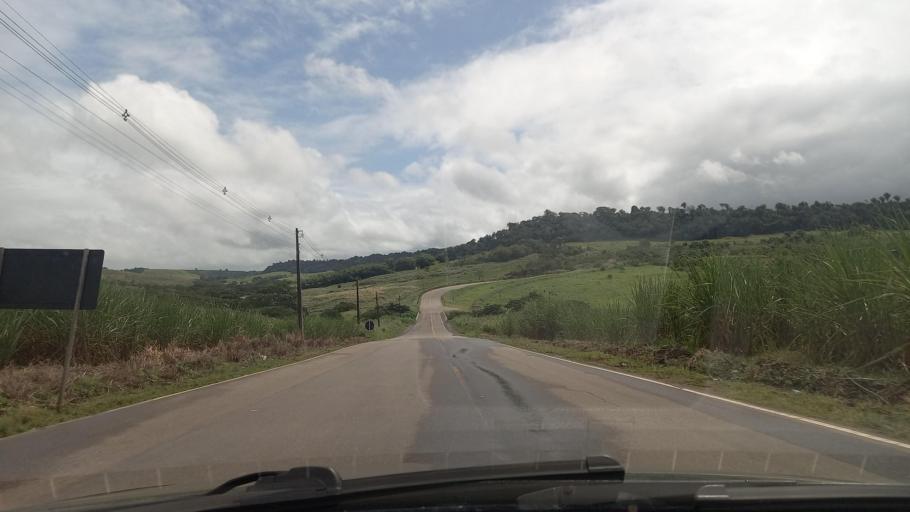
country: BR
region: Alagoas
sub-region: Sao Miguel Dos Campos
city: Sao Miguel dos Campos
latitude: -9.8162
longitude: -36.2203
